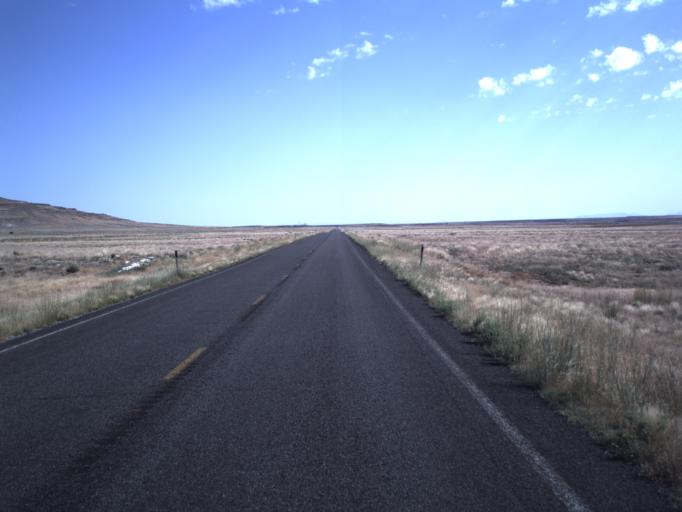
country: US
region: Utah
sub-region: Beaver County
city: Milford
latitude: 38.8540
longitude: -112.8410
